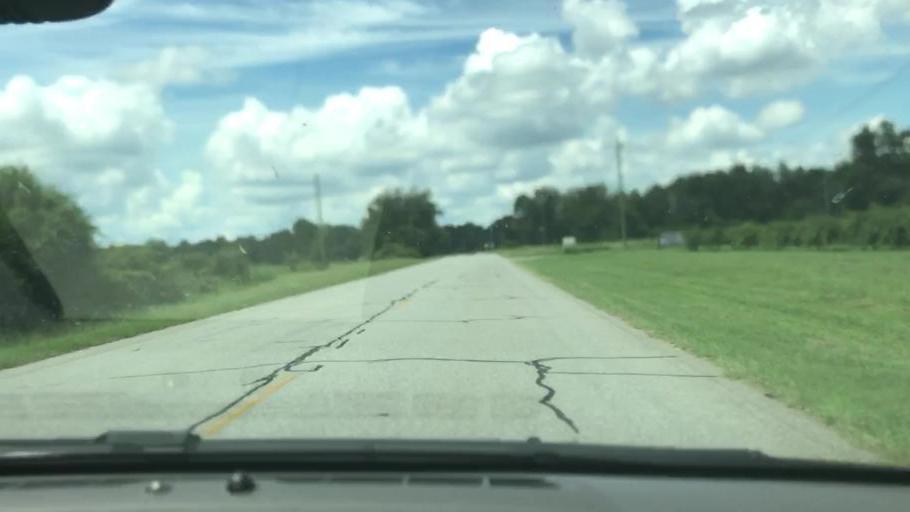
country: US
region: Georgia
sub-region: Stewart County
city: Lumpkin
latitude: 32.1415
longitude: -85.0082
